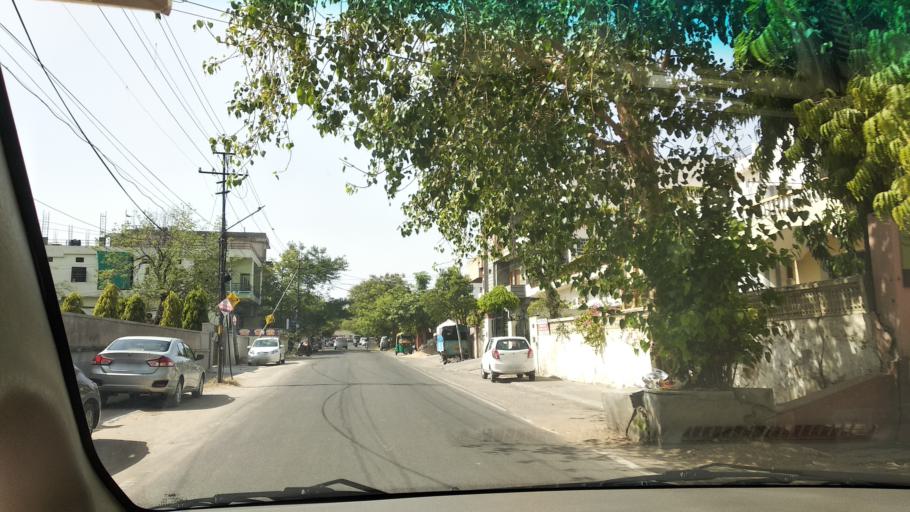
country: IN
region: Rajasthan
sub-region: Jaipur
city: Jaipur
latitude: 26.9152
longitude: 75.7945
